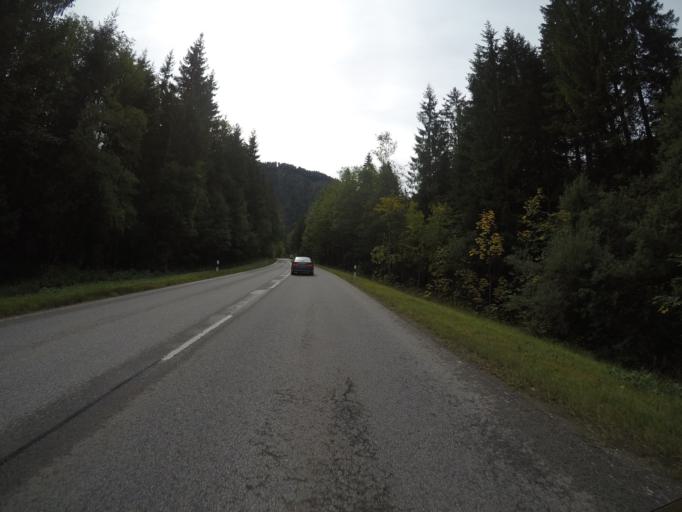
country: DE
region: Bavaria
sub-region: Upper Bavaria
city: Kreuth
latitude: 47.6301
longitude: 11.7455
